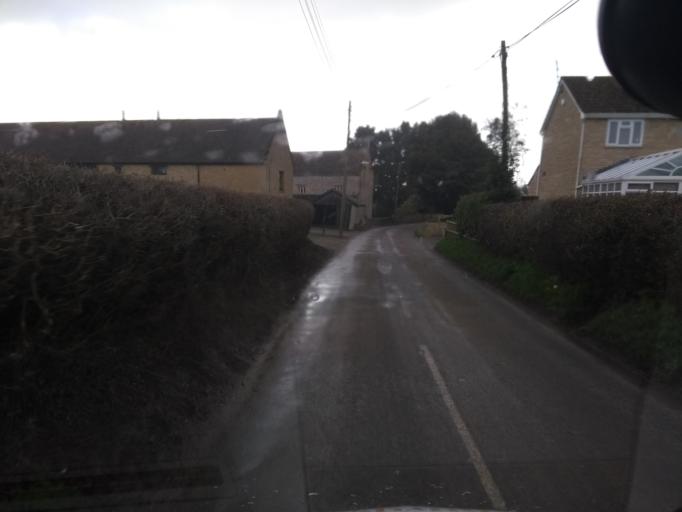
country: GB
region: England
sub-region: Somerset
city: South Petherton
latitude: 50.9787
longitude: -2.8193
